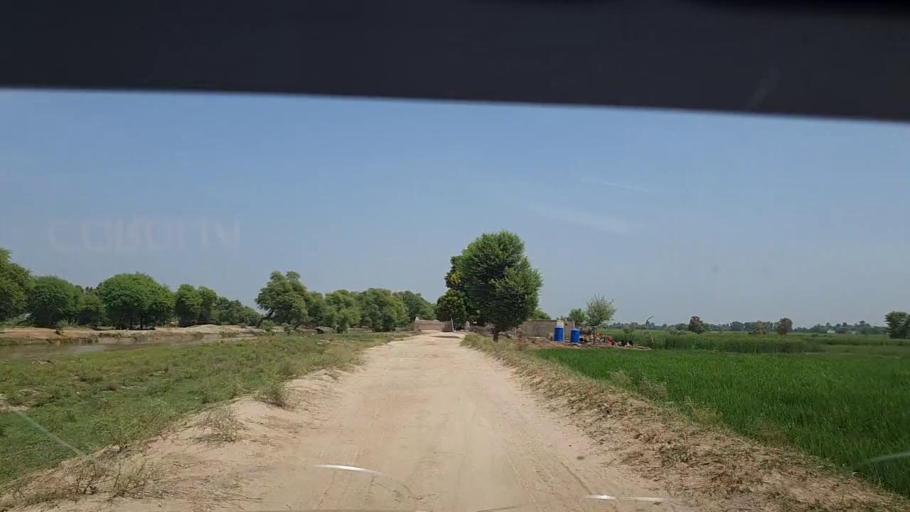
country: PK
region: Sindh
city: Tangwani
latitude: 28.2325
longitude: 68.9460
